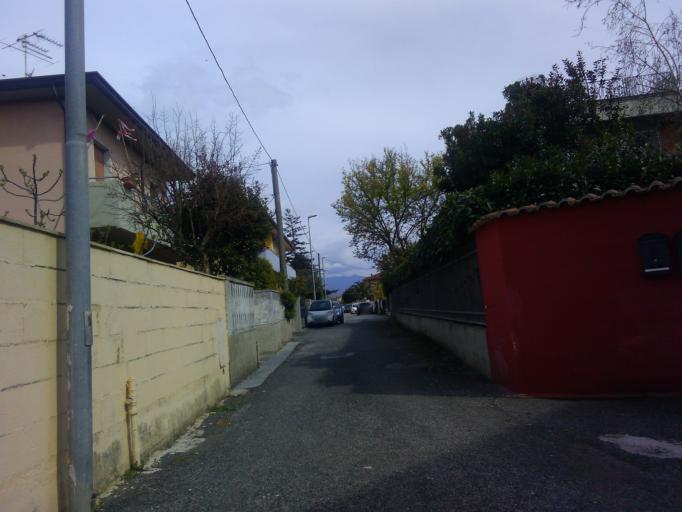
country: IT
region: Tuscany
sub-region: Provincia di Massa-Carrara
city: Marina di Carrara
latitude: 44.0488
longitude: 10.0248
